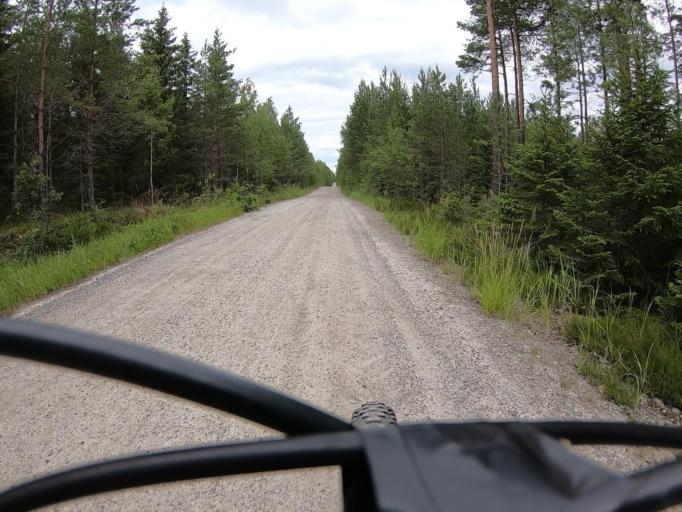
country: FI
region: Varsinais-Suomi
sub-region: Vakka-Suomi
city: Uusikaupunki
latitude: 60.8553
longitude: 21.3821
